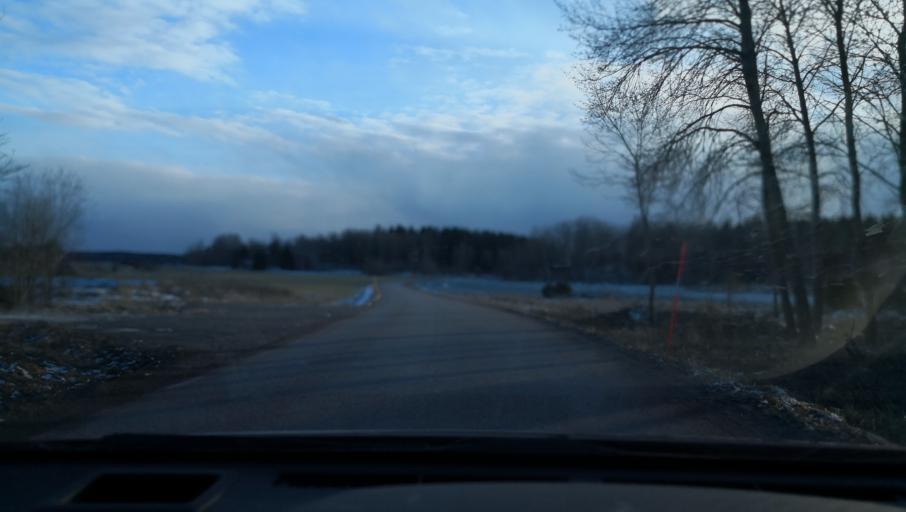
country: SE
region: Vaestmanland
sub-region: Vasteras
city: Tillberga
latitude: 59.6535
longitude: 16.7545
